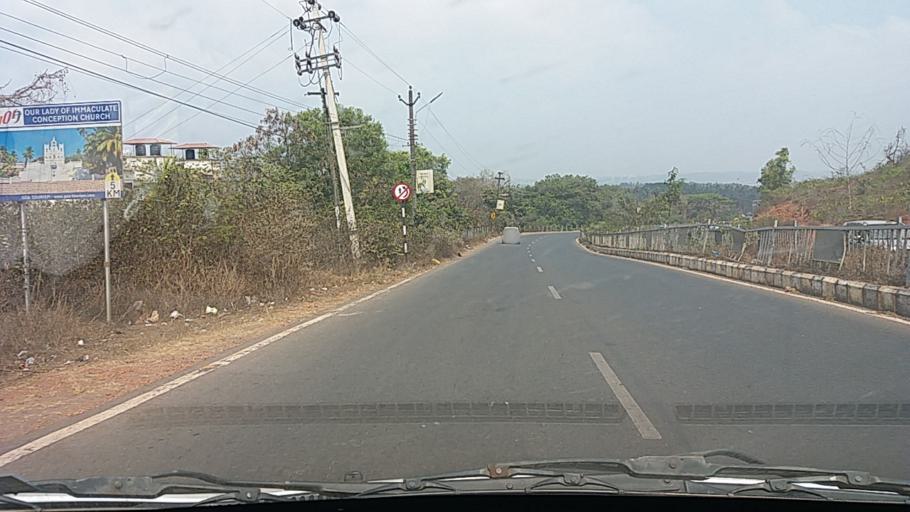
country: IN
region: Goa
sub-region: North Goa
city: Bambolim
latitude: 15.4665
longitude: 73.8515
